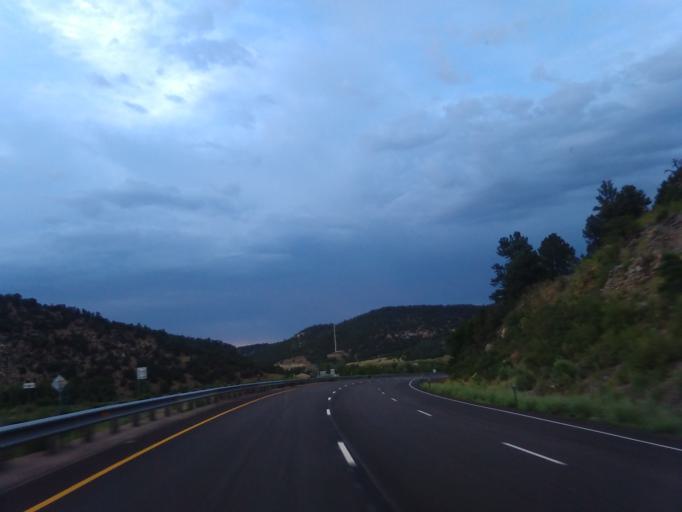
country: US
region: Colorado
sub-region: Las Animas County
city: Trinidad
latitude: 37.0879
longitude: -104.5224
